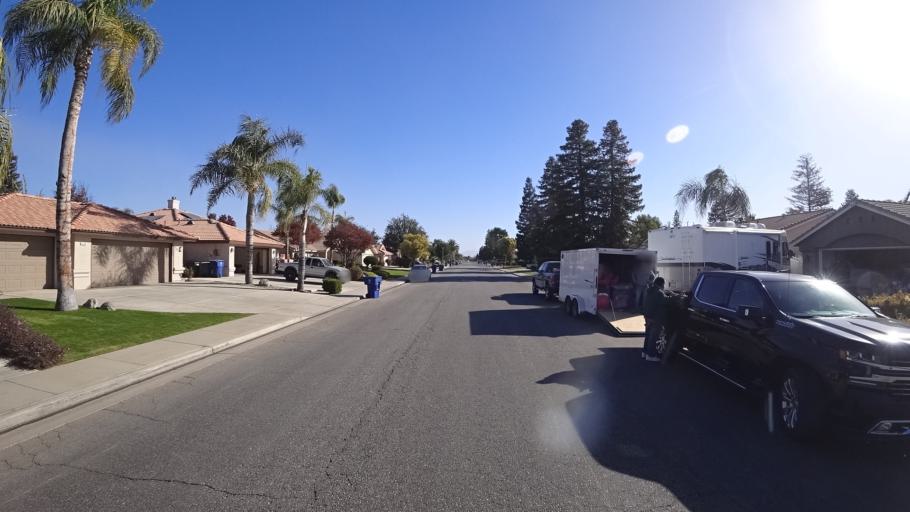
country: US
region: California
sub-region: Kern County
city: Greenfield
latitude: 35.2782
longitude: -119.0420
